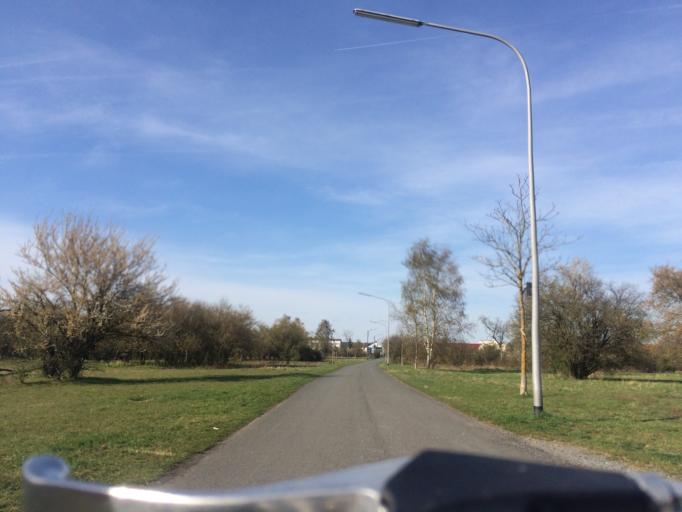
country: DE
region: Hesse
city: Morfelden-Walldorf
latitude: 49.9918
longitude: 8.5677
